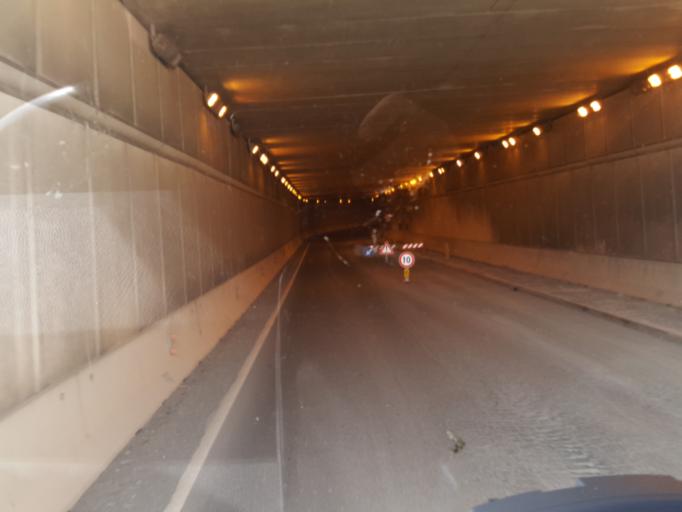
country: IT
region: Latium
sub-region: Citta metropolitana di Roma Capitale
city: Aurelia
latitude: 42.1260
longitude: 11.7846
